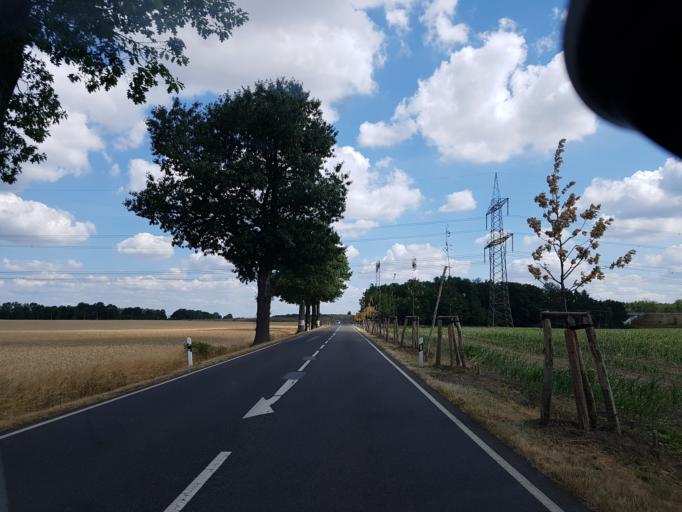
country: DE
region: Brandenburg
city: Drebkau
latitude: 51.6606
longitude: 14.2368
